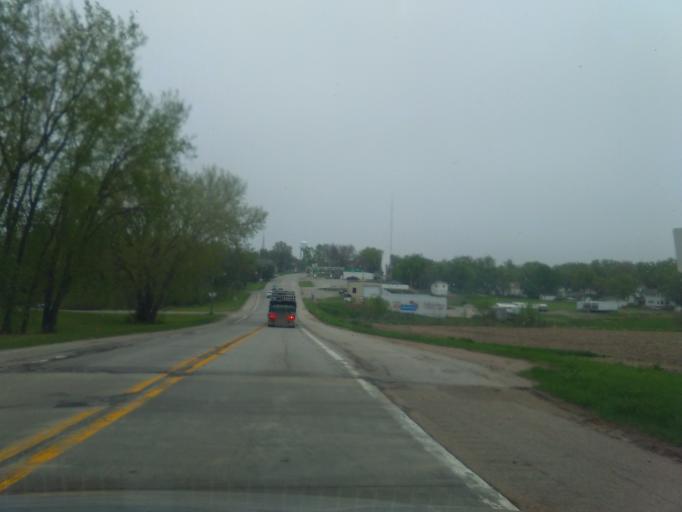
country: US
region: Nebraska
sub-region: Burt County
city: Oakland
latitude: 41.8302
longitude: -96.4629
